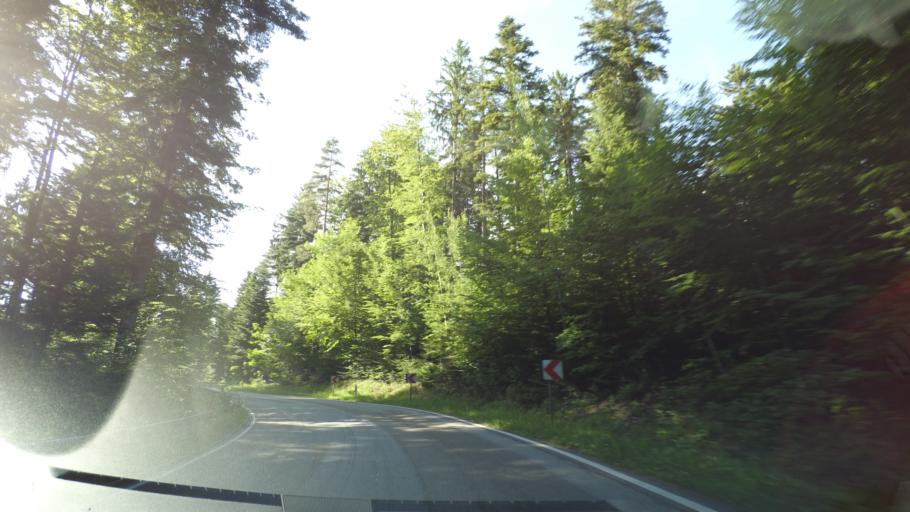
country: DE
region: Baden-Wuerttemberg
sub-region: Regierungsbezirk Stuttgart
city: Gschwend
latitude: 48.9305
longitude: 9.7083
